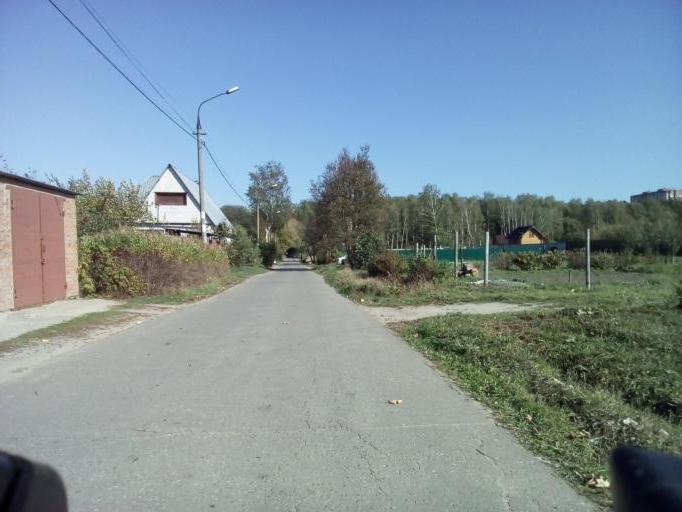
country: RU
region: Moskovskaya
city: Ramenskoye
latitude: 55.5453
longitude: 38.2989
